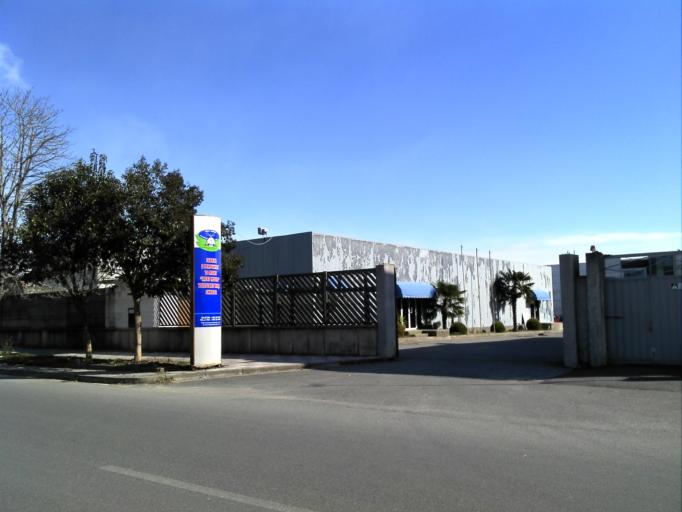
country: AL
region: Shkoder
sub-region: Rrethi i Shkodres
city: Shkoder
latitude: 42.0793
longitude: 19.5278
